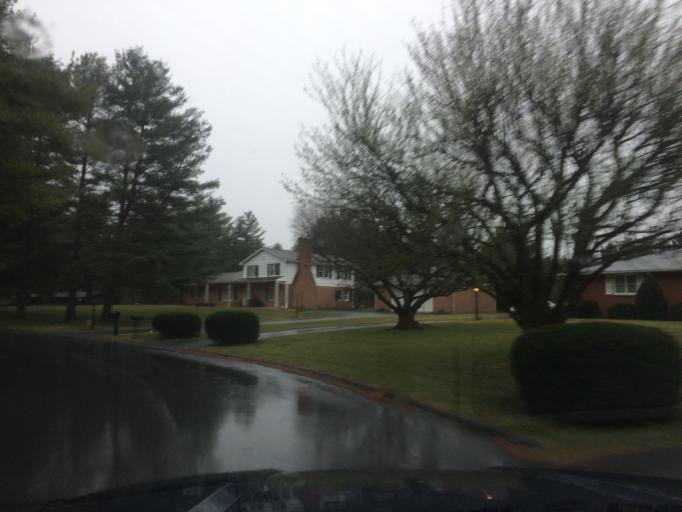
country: US
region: Maryland
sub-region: Carroll County
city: Eldersburg
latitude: 39.3744
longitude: -76.9145
